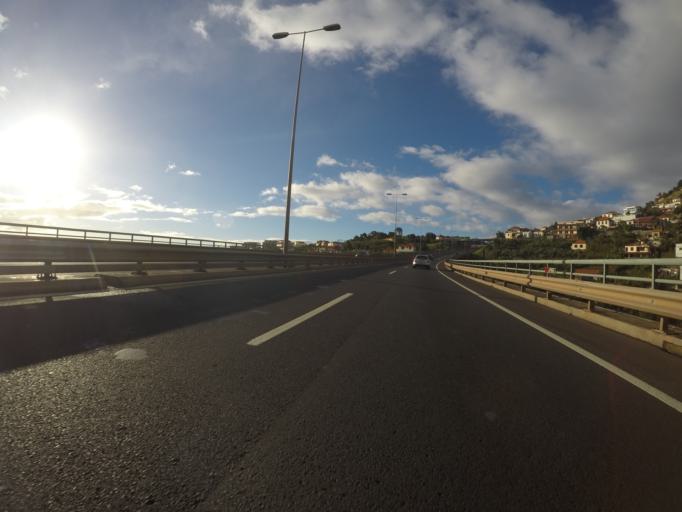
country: PT
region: Madeira
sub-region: Funchal
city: Nossa Senhora do Monte
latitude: 32.6598
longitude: -16.9340
